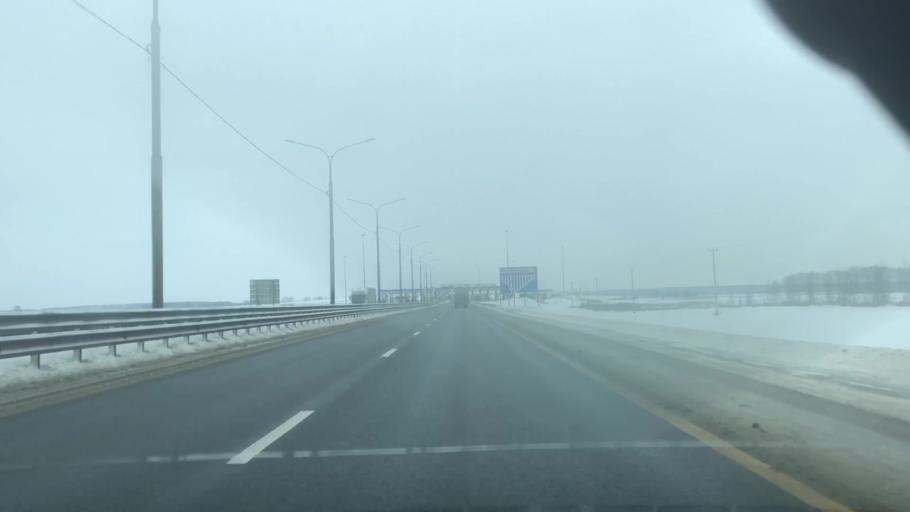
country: RU
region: Tula
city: Dubovka
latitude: 53.8828
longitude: 38.0507
